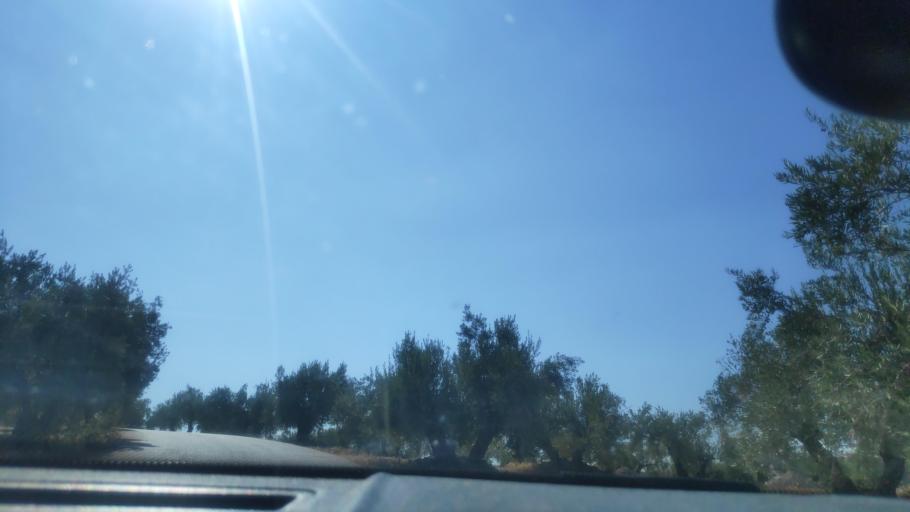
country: ES
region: Andalusia
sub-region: Provincia de Jaen
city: Jaen
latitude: 37.8294
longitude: -3.7613
